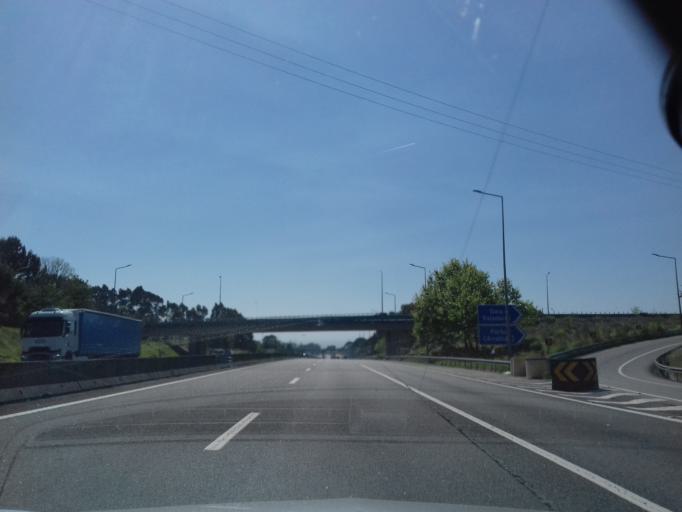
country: PT
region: Porto
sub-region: Vila Nova de Gaia
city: Gulpilhares
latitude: 41.0811
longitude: -8.6291
